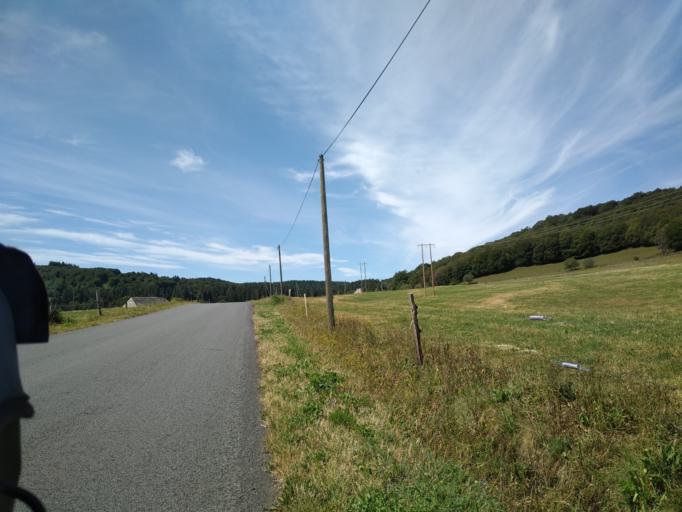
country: FR
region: Midi-Pyrenees
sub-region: Departement de l'Aveyron
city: Laguiole
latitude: 44.6766
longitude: 2.9875
